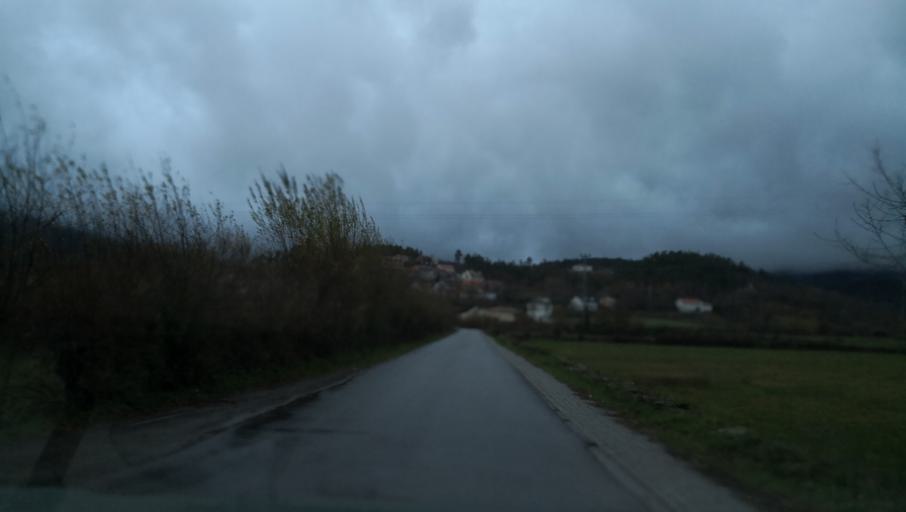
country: PT
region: Vila Real
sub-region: Santa Marta de Penaguiao
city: Santa Marta de Penaguiao
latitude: 41.2960
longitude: -7.8722
